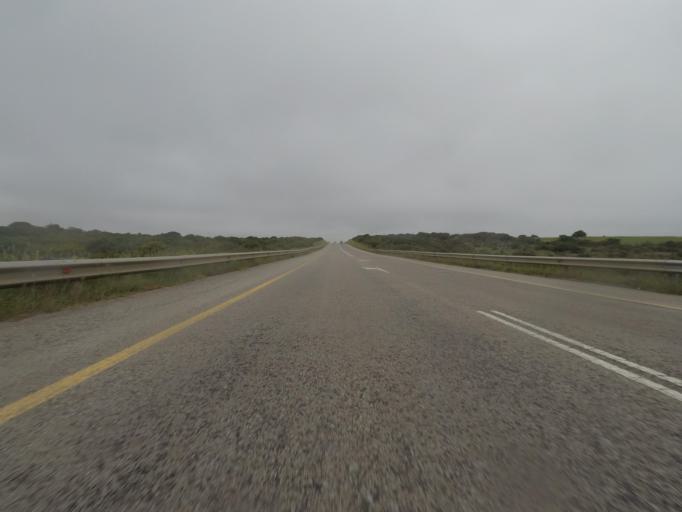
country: ZA
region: Eastern Cape
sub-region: Cacadu District Municipality
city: Grahamstown
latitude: -33.6487
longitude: 26.3868
